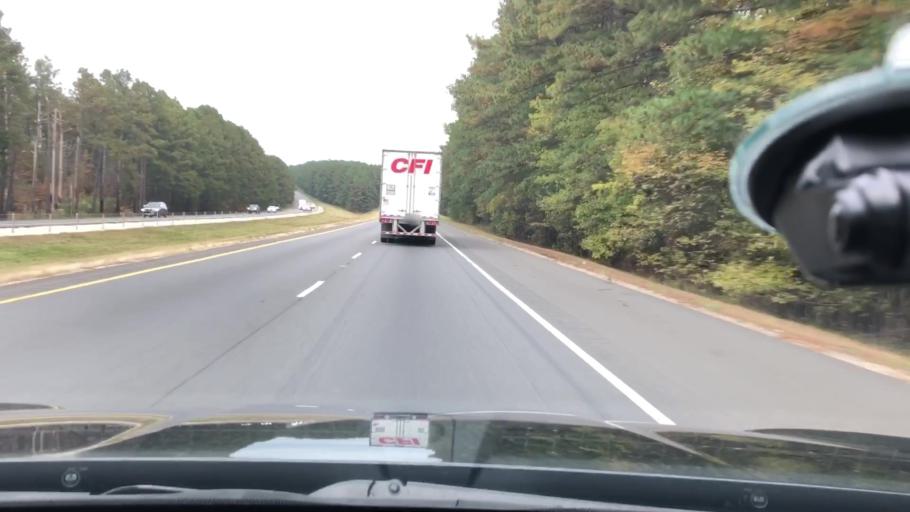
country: US
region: Arkansas
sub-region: Hot Spring County
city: Malvern
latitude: 34.2803
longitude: -92.9612
